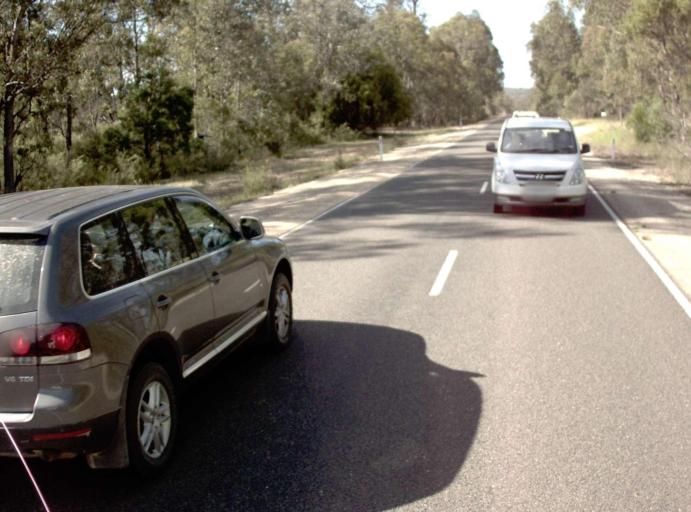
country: AU
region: Victoria
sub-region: East Gippsland
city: Lakes Entrance
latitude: -37.5882
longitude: 148.1230
